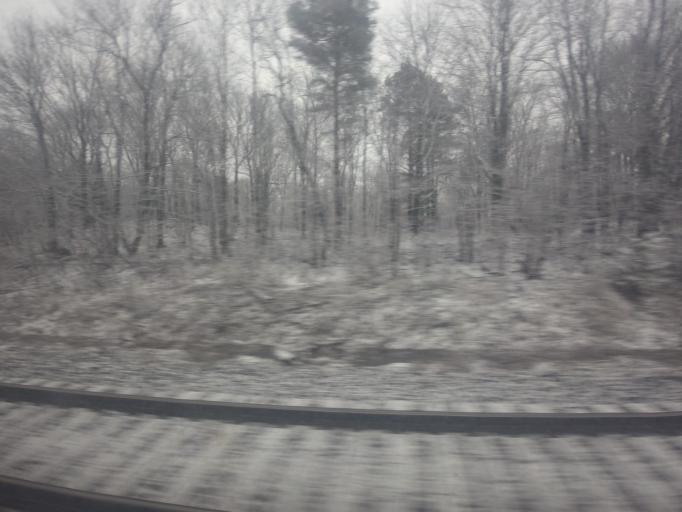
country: US
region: New York
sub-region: Jefferson County
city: Alexandria Bay
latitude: 44.4811
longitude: -75.8842
